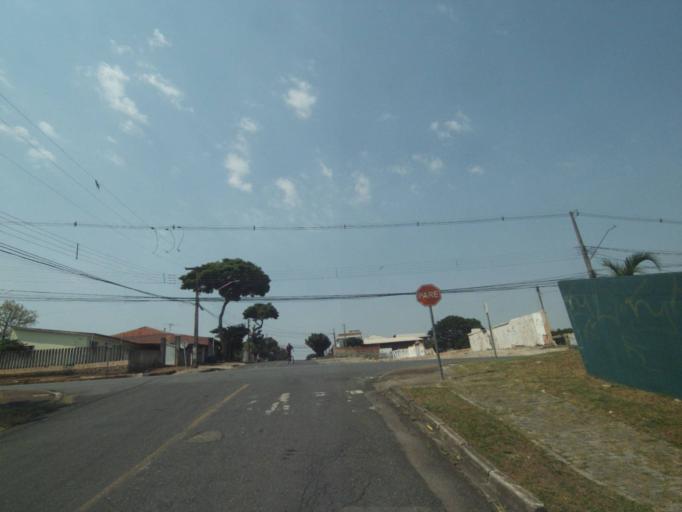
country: BR
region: Parana
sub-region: Sao Jose Dos Pinhais
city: Sao Jose dos Pinhais
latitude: -25.5351
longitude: -49.2495
